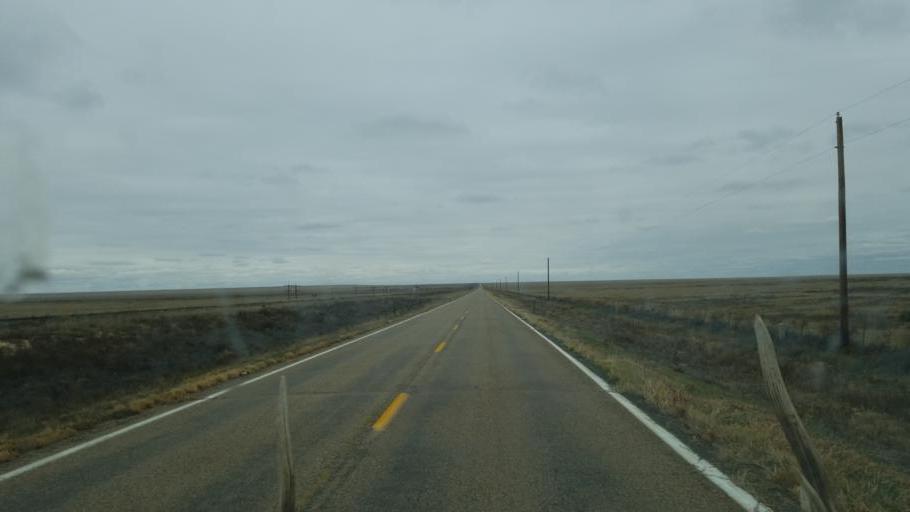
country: US
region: Colorado
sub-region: Crowley County
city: Ordway
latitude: 38.2432
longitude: -103.6164
